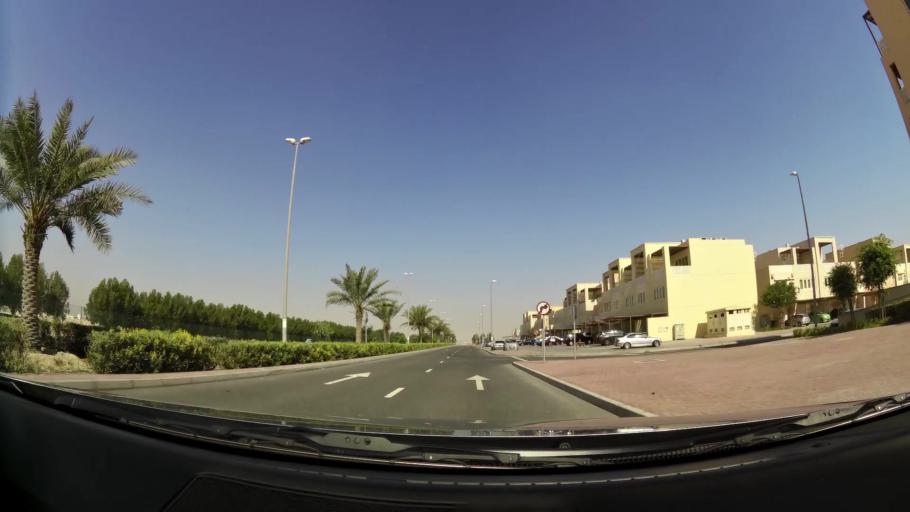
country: AE
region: Dubai
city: Dubai
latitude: 24.9494
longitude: 55.0492
